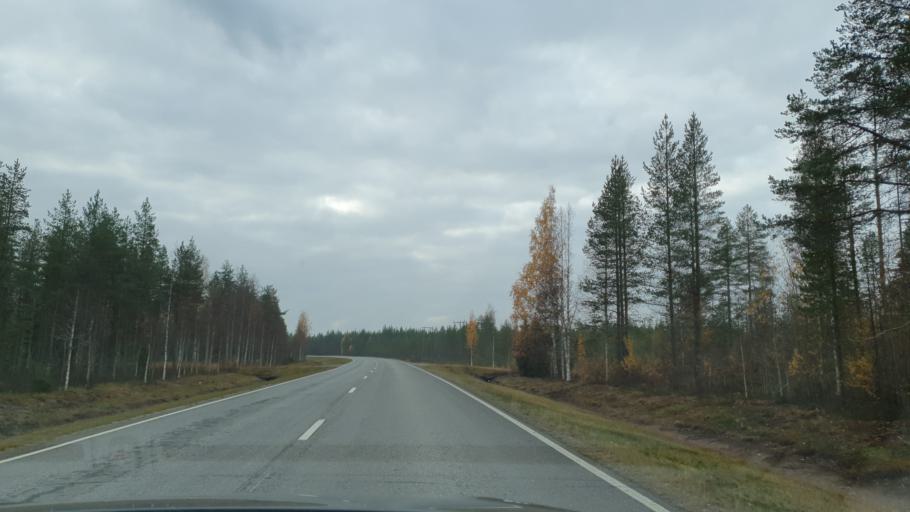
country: FI
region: Lapland
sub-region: Rovaniemi
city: Ranua
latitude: 66.0267
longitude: 26.3225
